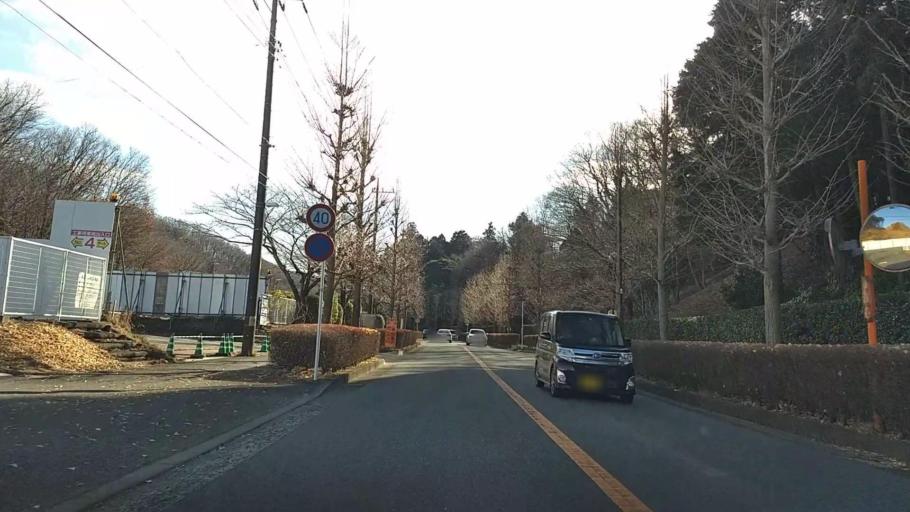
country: JP
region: Kanagawa
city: Atsugi
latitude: 35.4472
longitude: 139.3136
